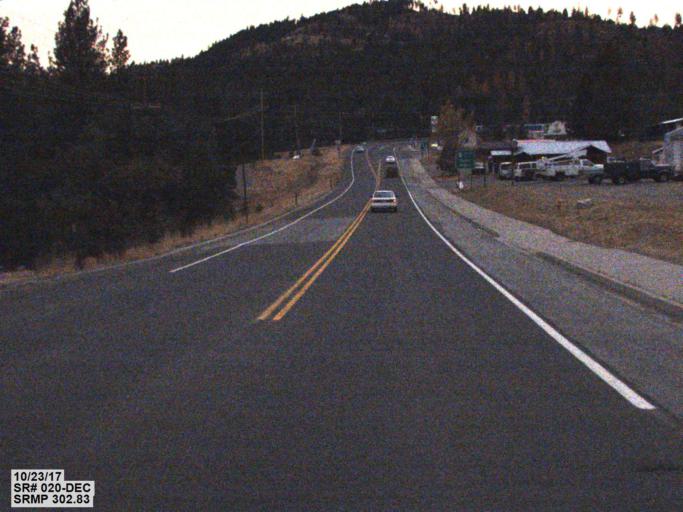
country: US
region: Washington
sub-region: Ferry County
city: Republic
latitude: 48.6417
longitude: -118.7306
